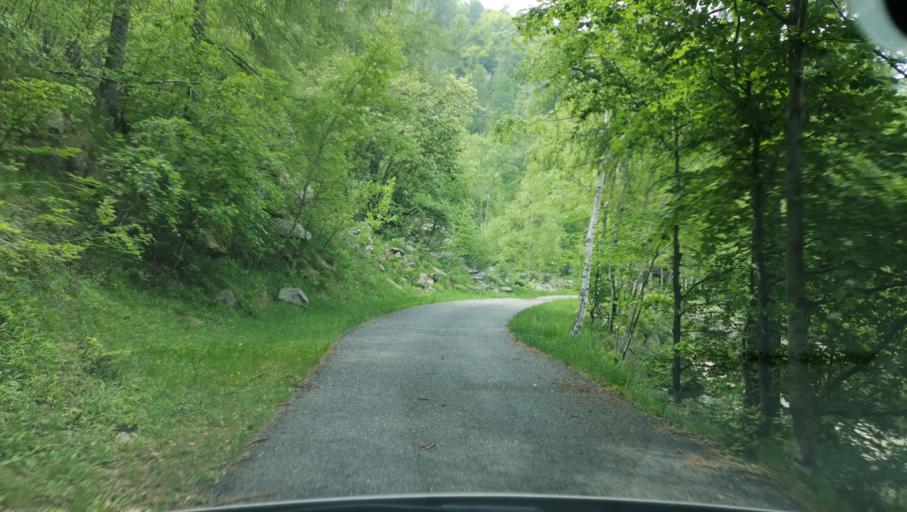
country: IT
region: Piedmont
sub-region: Provincia di Torino
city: Quincinetto
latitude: 45.5388
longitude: 7.7900
